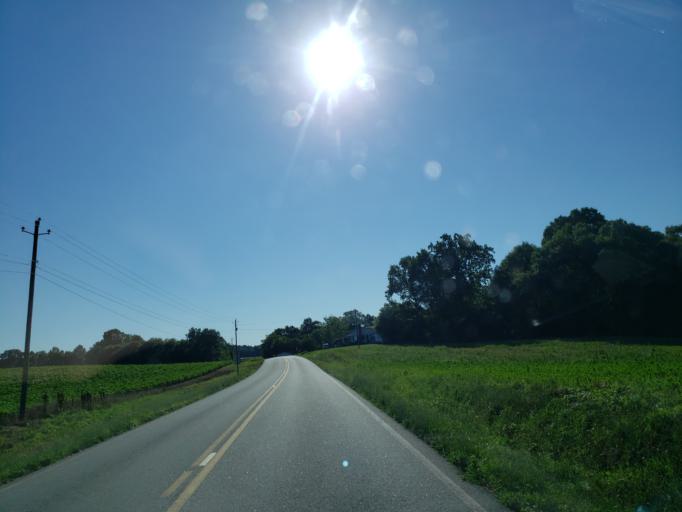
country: US
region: Georgia
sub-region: Bartow County
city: Euharlee
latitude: 34.1087
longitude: -84.9470
